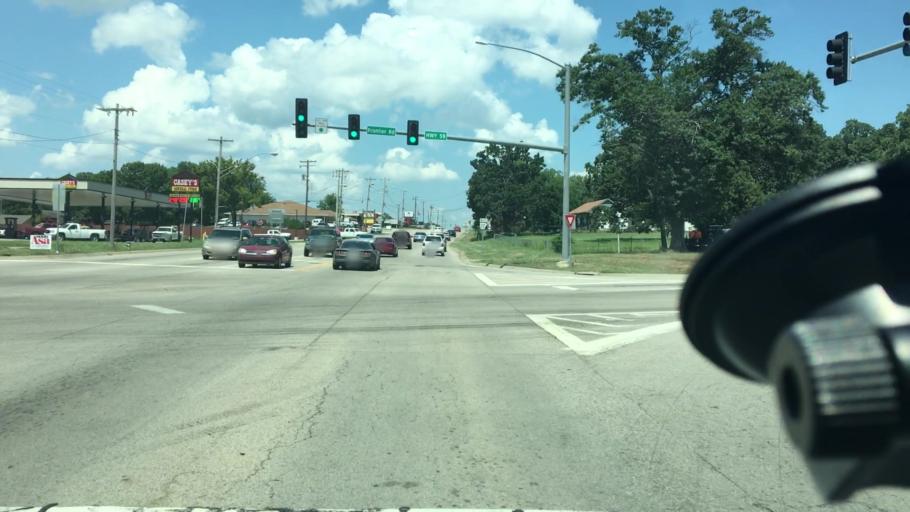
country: US
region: Arkansas
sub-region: Sebastian County
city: Barling
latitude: 35.3231
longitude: -94.2964
